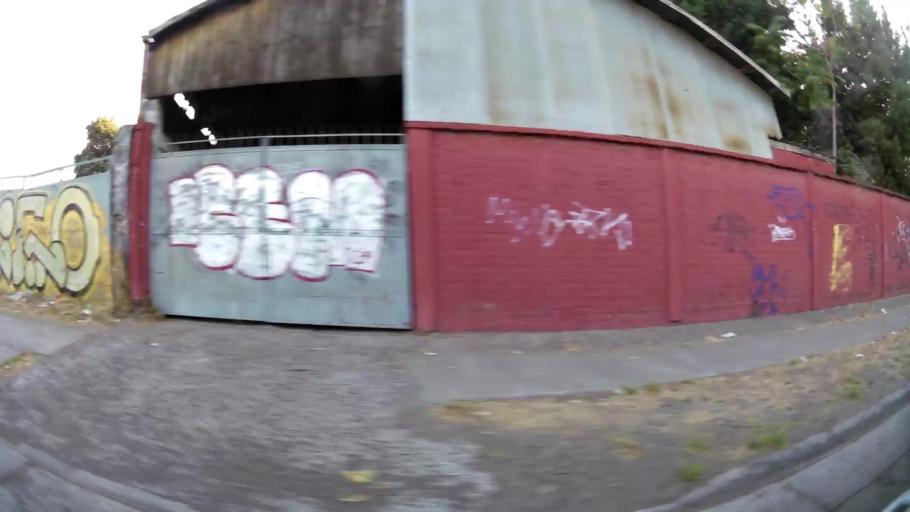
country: CL
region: Maule
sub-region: Provincia de Talca
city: Talca
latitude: -35.4469
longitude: -71.6664
